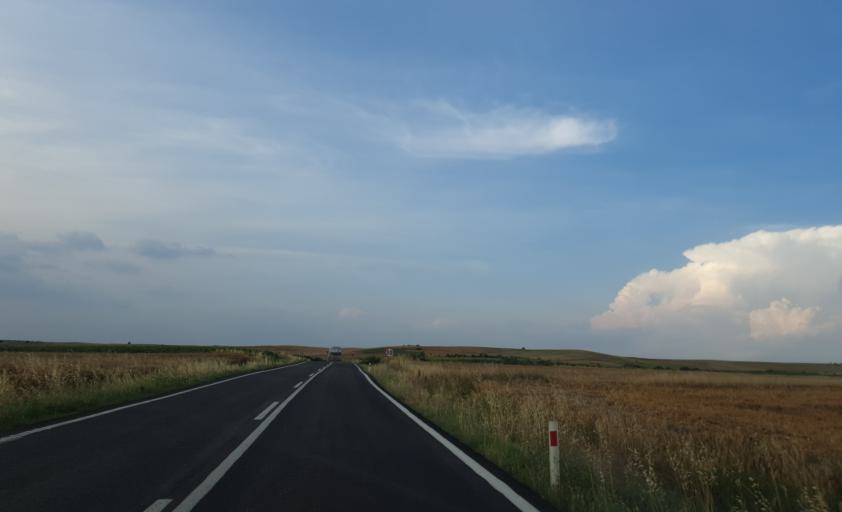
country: TR
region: Tekirdag
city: Hayrabolu
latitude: 41.2485
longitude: 27.1369
